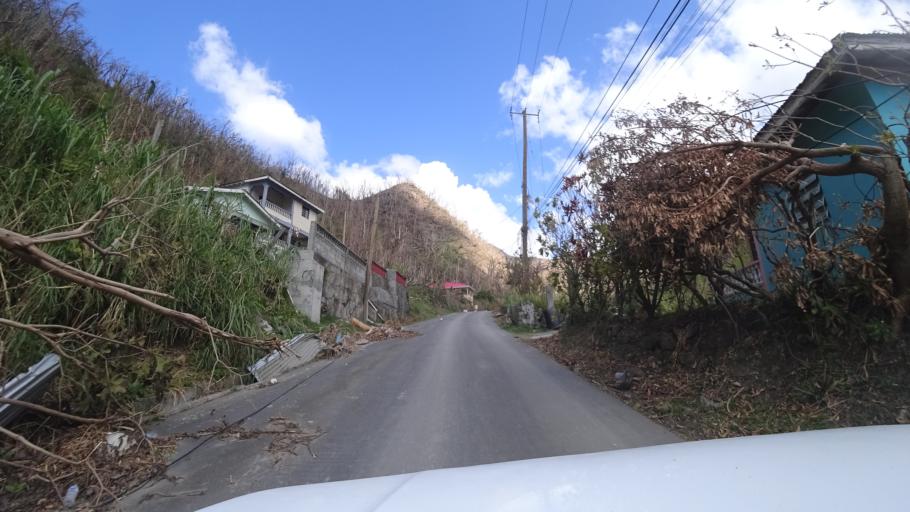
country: DM
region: Saint Luke
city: Pointe Michel
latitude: 15.2756
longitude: -61.3636
